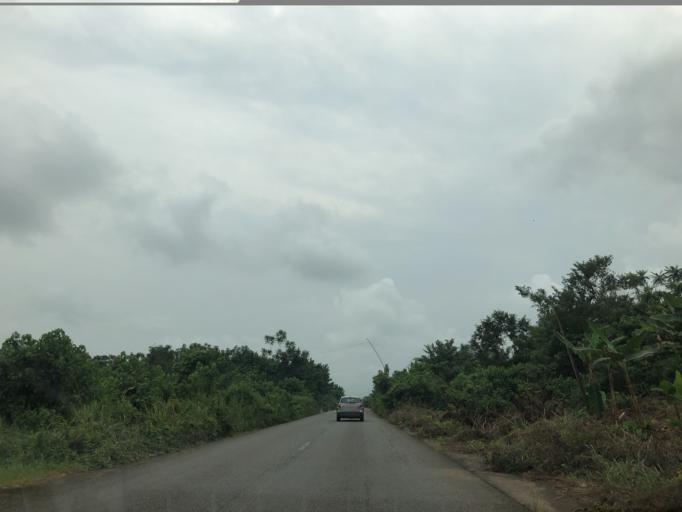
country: CM
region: Littoral
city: Dizangue
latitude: 3.4920
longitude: 10.1219
